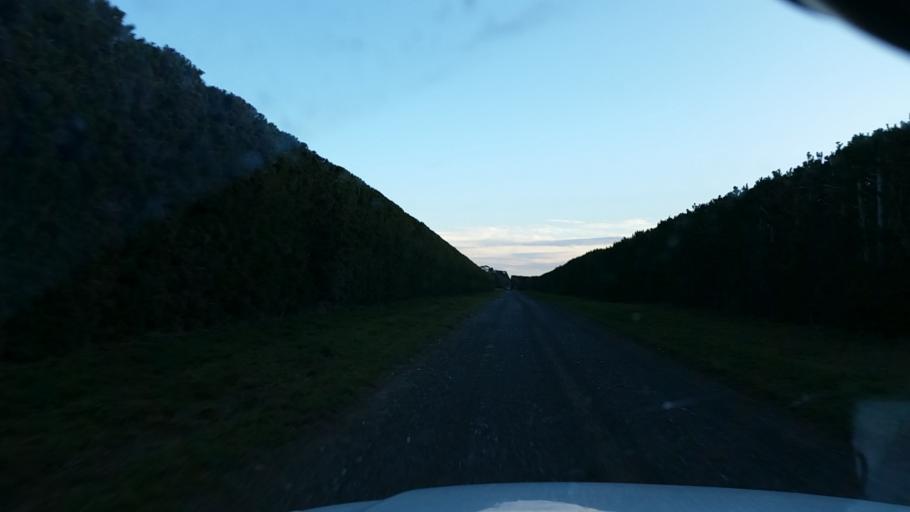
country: NZ
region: Canterbury
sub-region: Ashburton District
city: Tinwald
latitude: -43.9078
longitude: 171.5484
